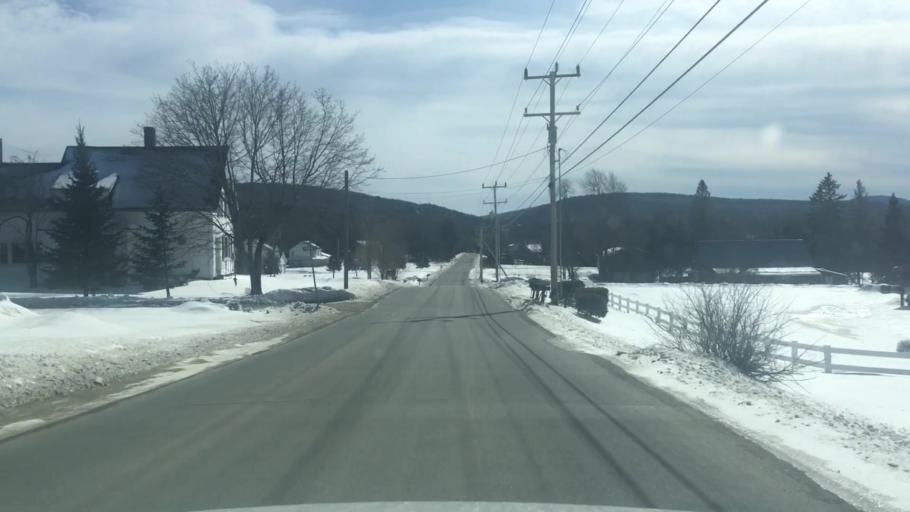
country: US
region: Maine
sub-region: Penobscot County
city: Holden
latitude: 44.7461
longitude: -68.6315
